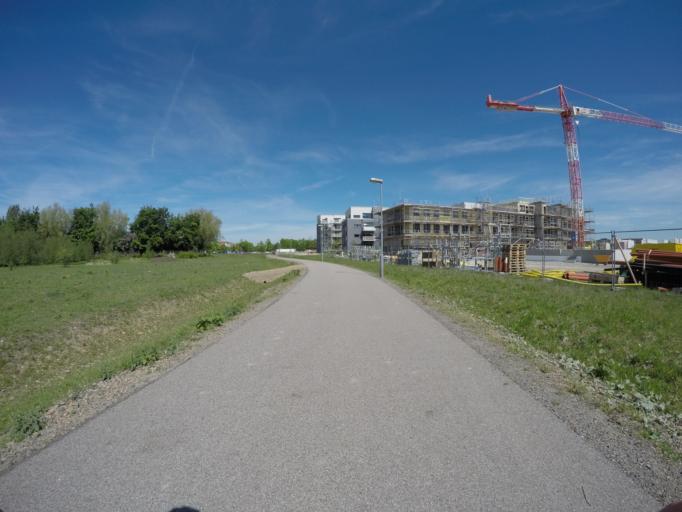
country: SE
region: Skane
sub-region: Malmo
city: Bunkeflostrand
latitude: 55.5693
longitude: 12.9741
